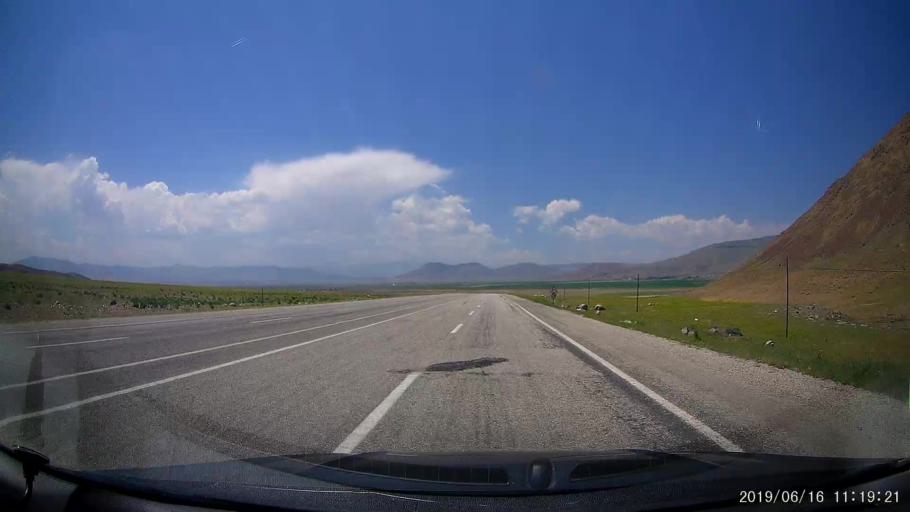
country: TR
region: Agri
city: Dogubayazit
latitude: 39.6996
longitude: 44.1152
